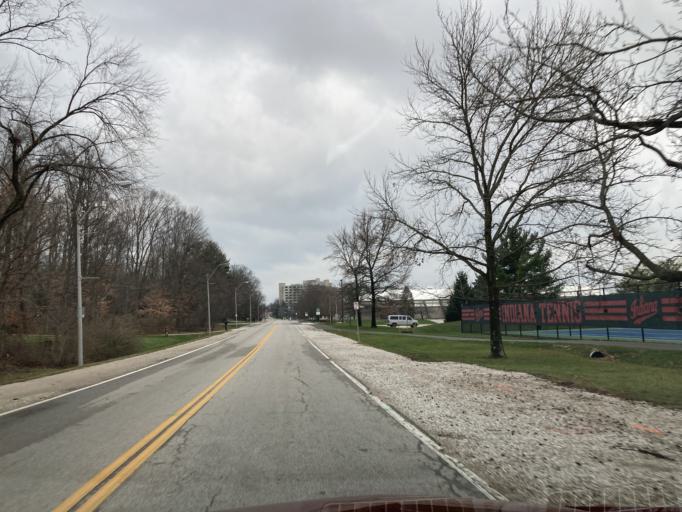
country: US
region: Indiana
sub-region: Monroe County
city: Bloomington
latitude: 39.1835
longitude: -86.5192
